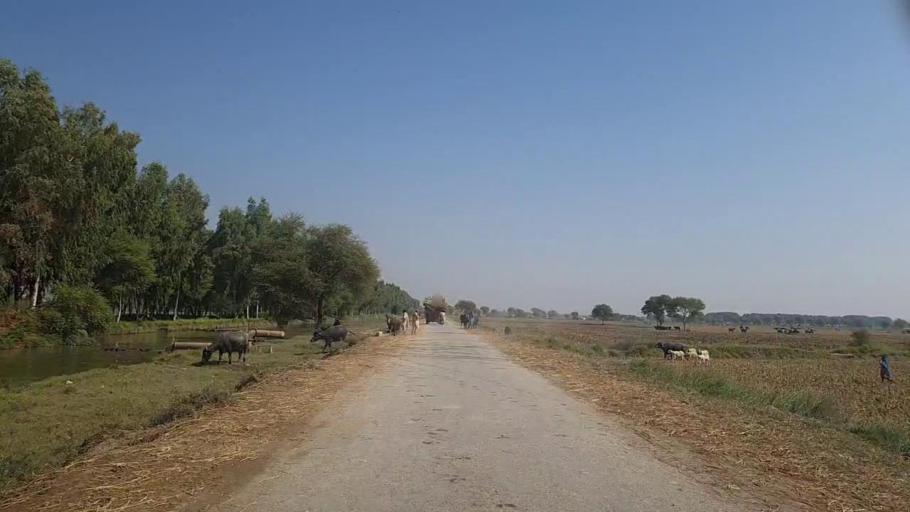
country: PK
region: Sindh
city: Thul
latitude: 28.2387
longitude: 68.7928
